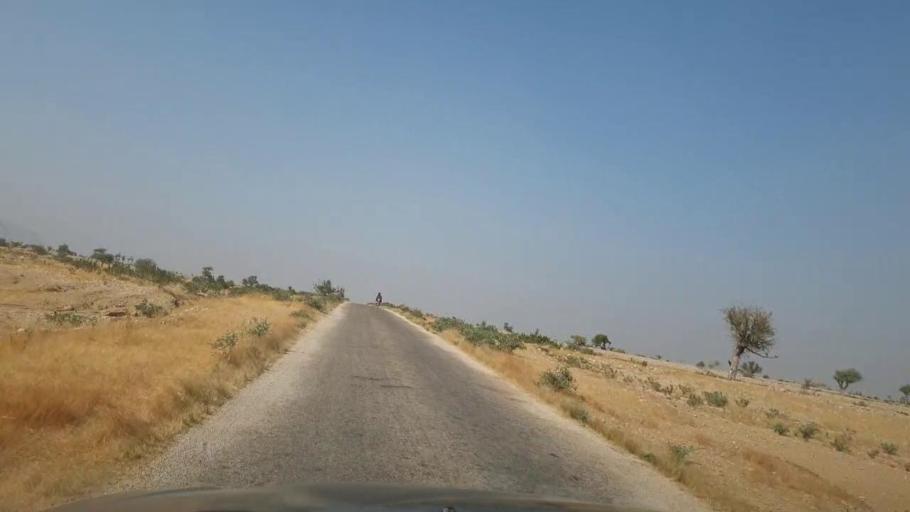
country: PK
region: Sindh
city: Jamshoro
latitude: 25.5997
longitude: 67.8163
